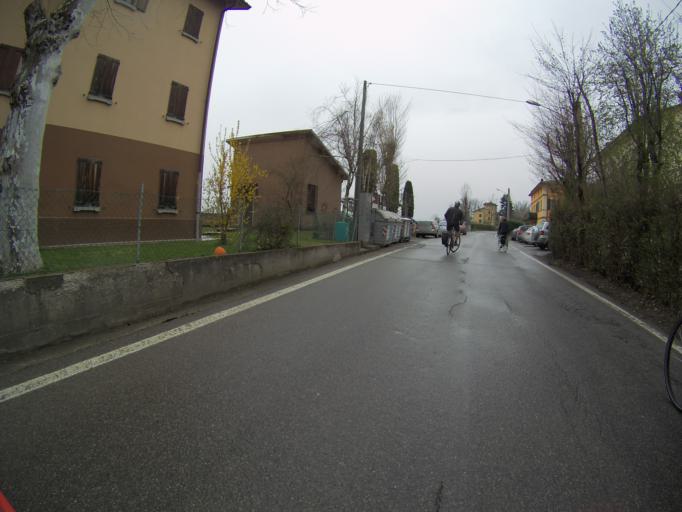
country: IT
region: Emilia-Romagna
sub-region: Provincia di Reggio Emilia
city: Ciano d'Enza
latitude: 44.5363
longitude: 10.4157
